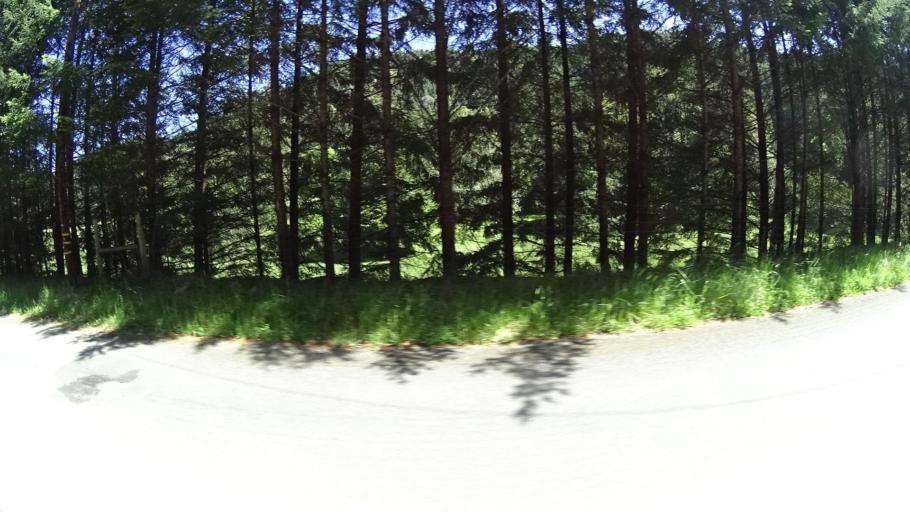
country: US
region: California
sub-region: Humboldt County
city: Rio Dell
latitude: 40.2666
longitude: -124.1983
